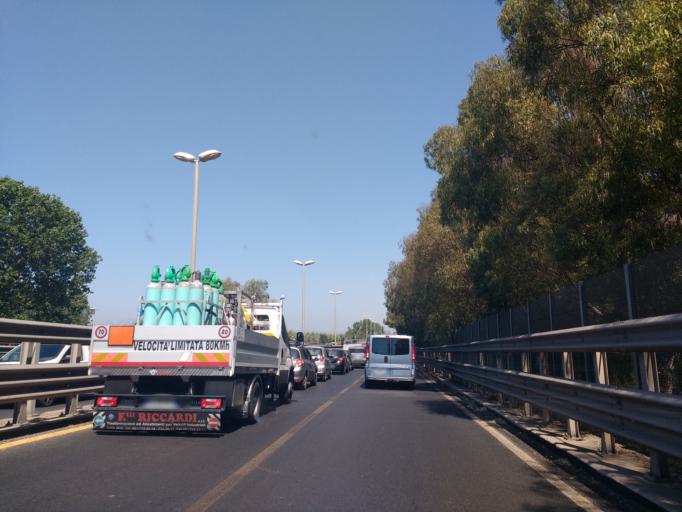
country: IT
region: Latium
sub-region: Citta metropolitana di Roma Capitale
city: Fiumicino-Isola Sacra
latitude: 41.7754
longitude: 12.2536
